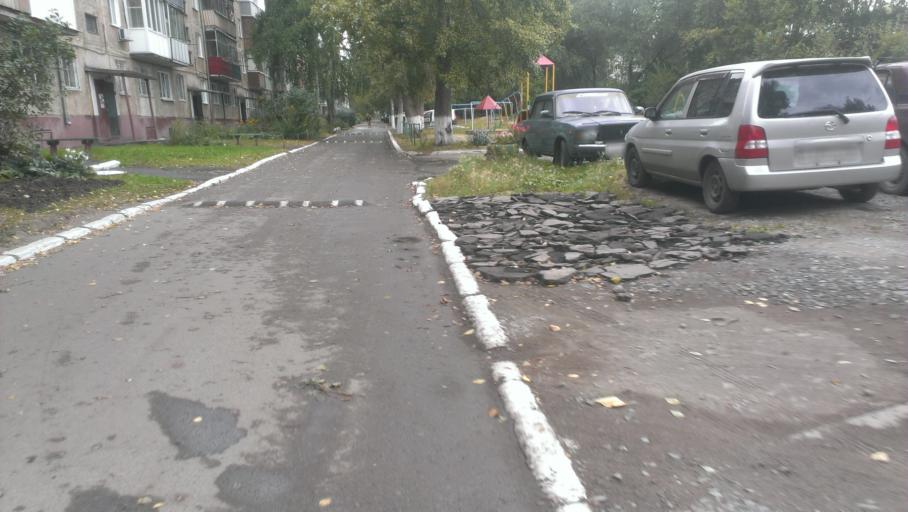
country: RU
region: Altai Krai
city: Novosilikatnyy
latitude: 53.3725
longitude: 83.6748
